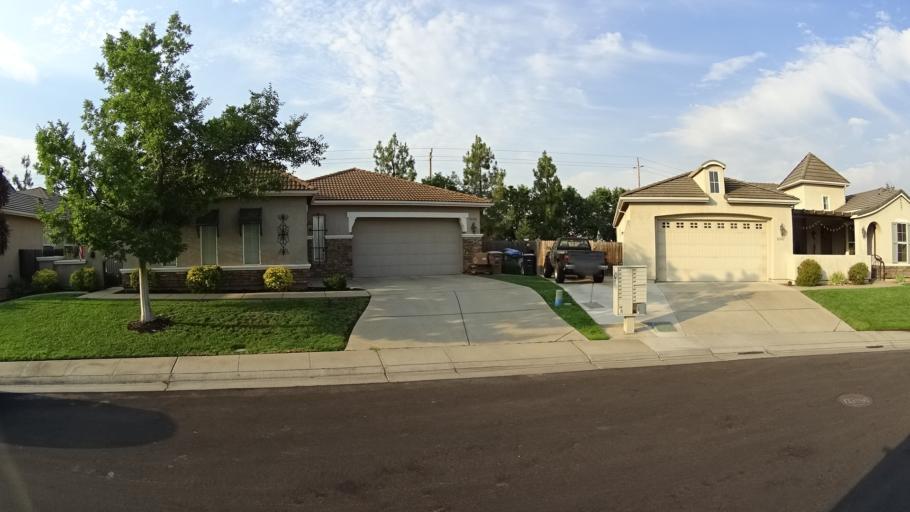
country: US
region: California
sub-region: Sacramento County
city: Laguna
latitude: 38.3799
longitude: -121.4356
